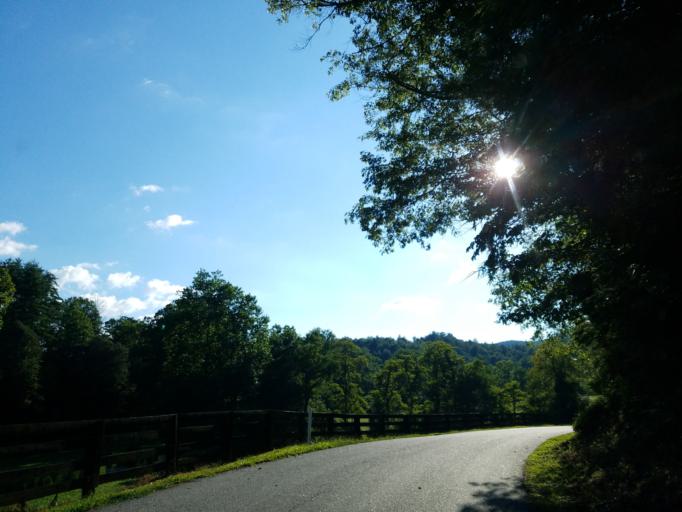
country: US
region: Georgia
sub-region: Union County
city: Blairsville
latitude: 34.7608
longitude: -84.1032
